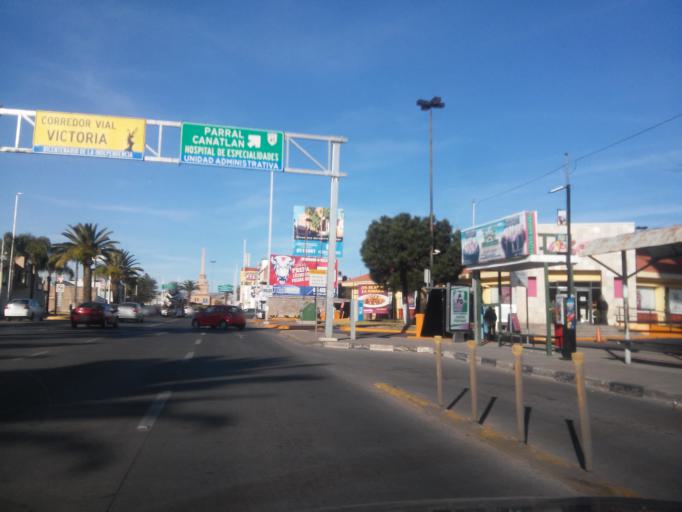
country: MX
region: Durango
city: Victoria de Durango
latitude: 24.0351
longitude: -104.6550
